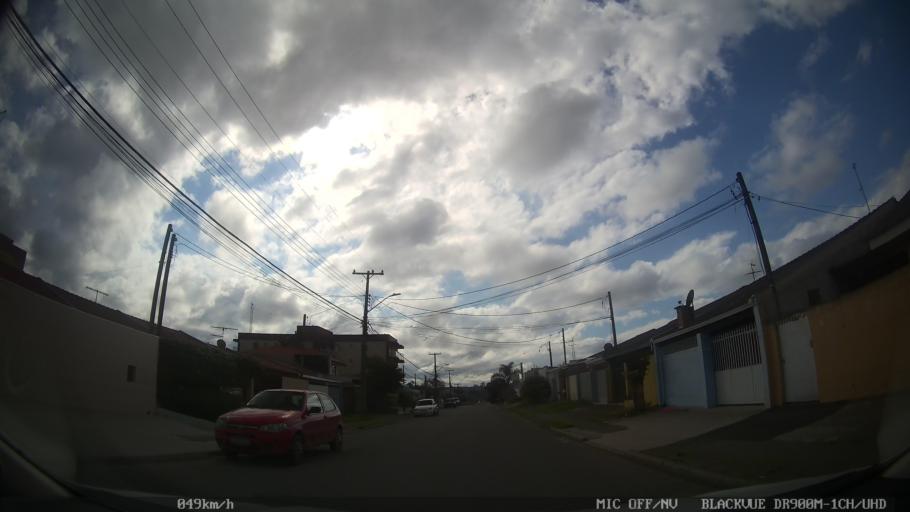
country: BR
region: Parana
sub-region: Colombo
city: Colombo
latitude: -25.3476
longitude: -49.1939
